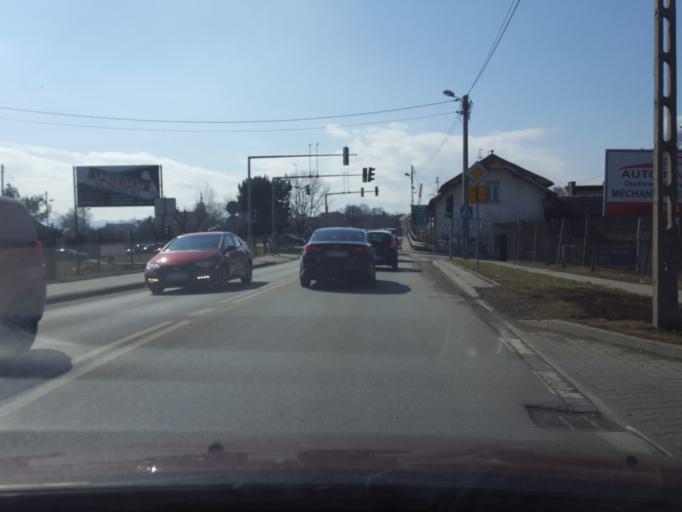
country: PL
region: Lesser Poland Voivodeship
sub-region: Powiat nowosadecki
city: Nowy Sacz
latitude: 49.6318
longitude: 20.6917
